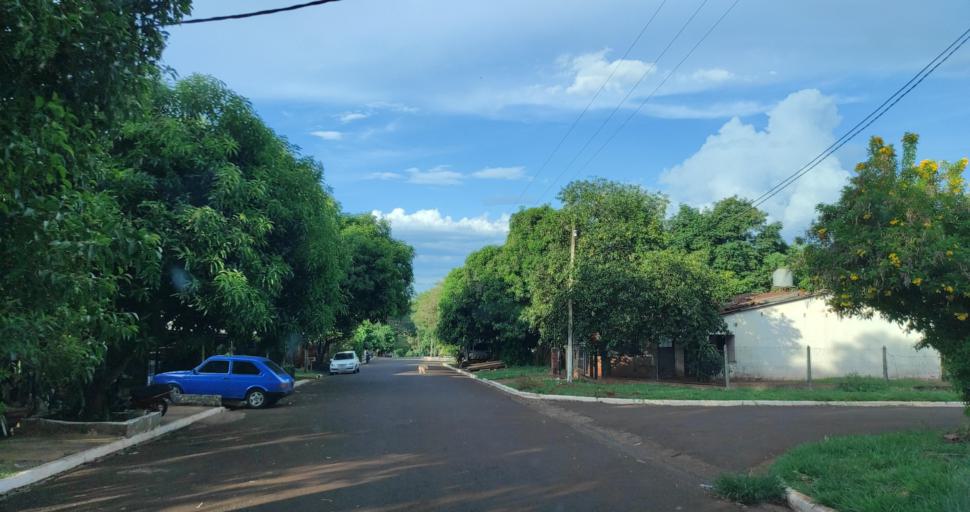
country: AR
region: Misiones
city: Santo Pipo
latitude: -27.1399
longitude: -55.4117
